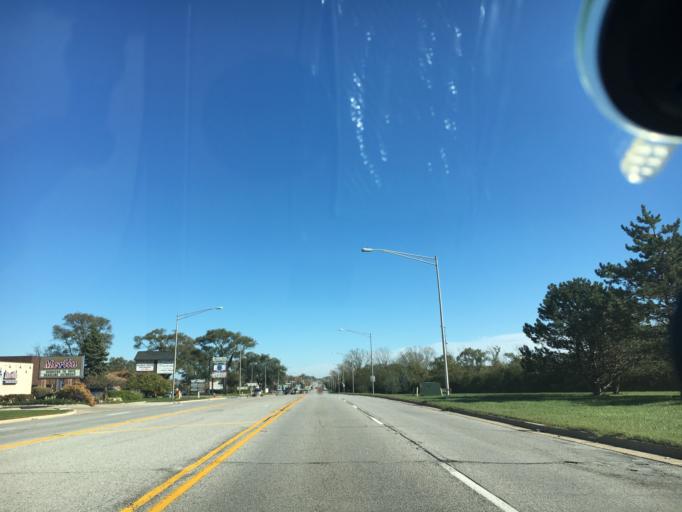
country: US
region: Illinois
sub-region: Cook County
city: Oak Forest
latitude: 41.6027
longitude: -87.7670
